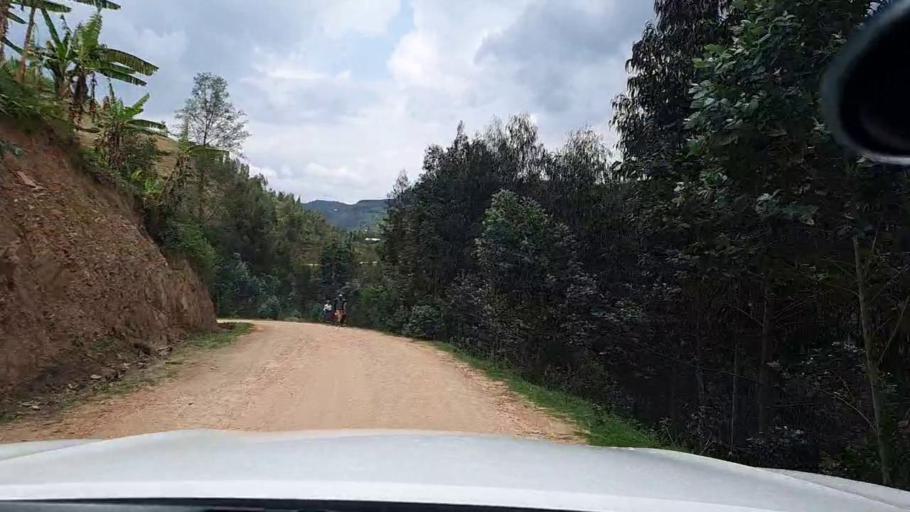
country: RW
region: Western Province
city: Kibuye
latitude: -2.1219
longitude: 29.4248
